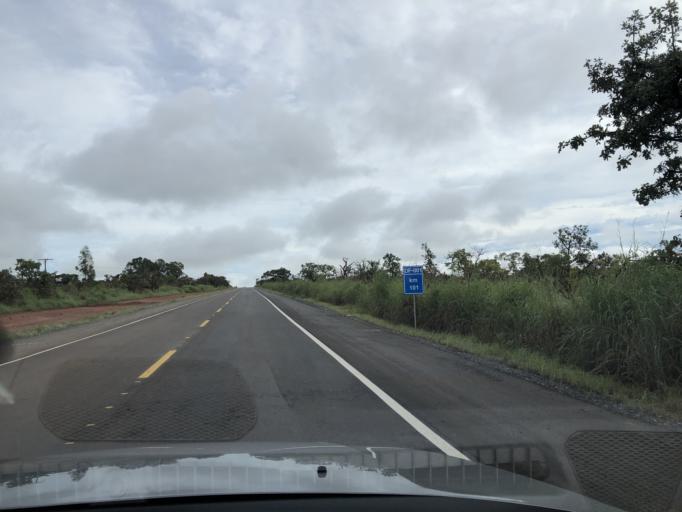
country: BR
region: Federal District
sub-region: Brasilia
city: Brasilia
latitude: -15.6402
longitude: -48.0789
